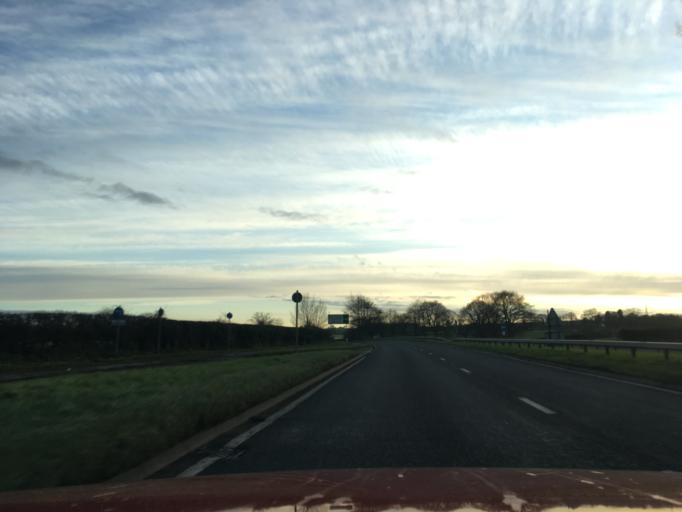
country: GB
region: England
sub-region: Staffordshire
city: Stone
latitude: 52.8827
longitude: -2.1329
